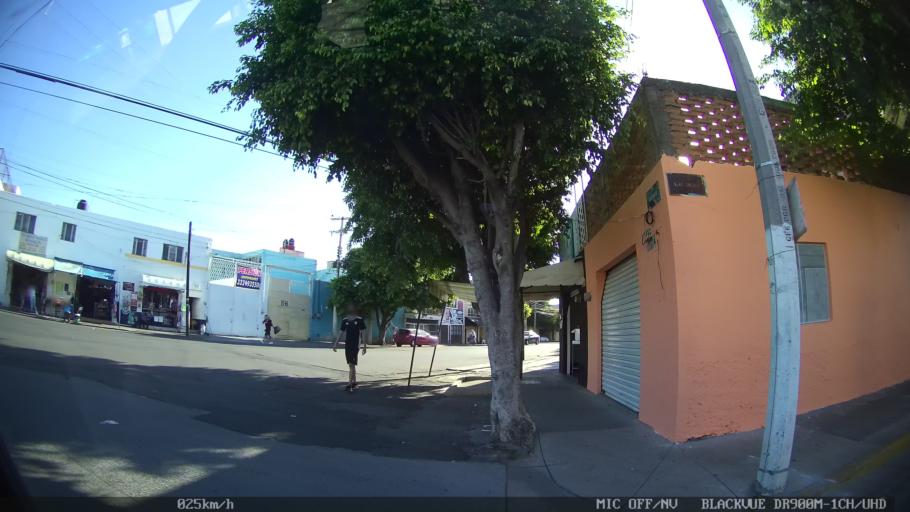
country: MX
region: Jalisco
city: Tlaquepaque
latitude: 20.7080
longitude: -103.2982
